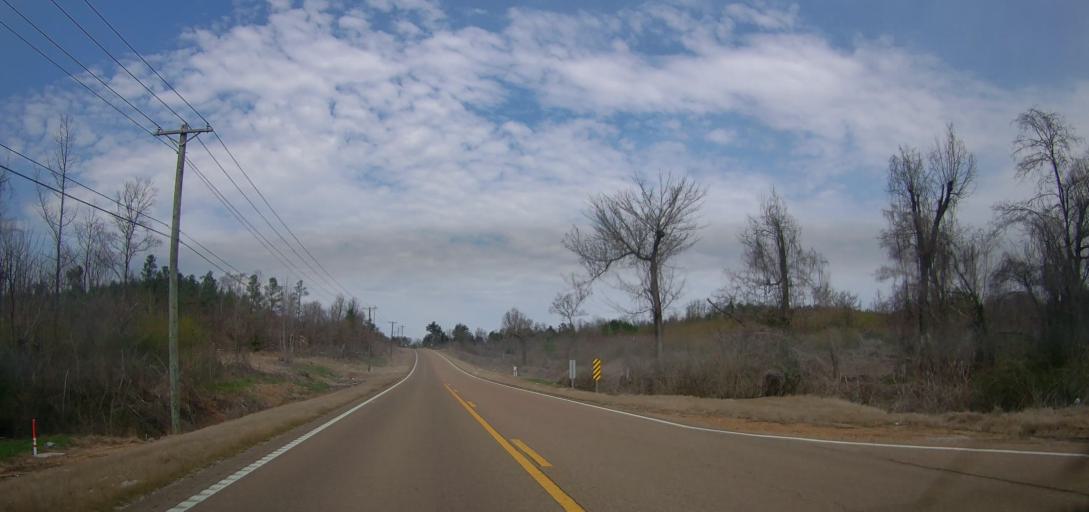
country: US
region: Mississippi
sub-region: Marshall County
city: Holly Springs
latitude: 34.7458
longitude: -89.4270
